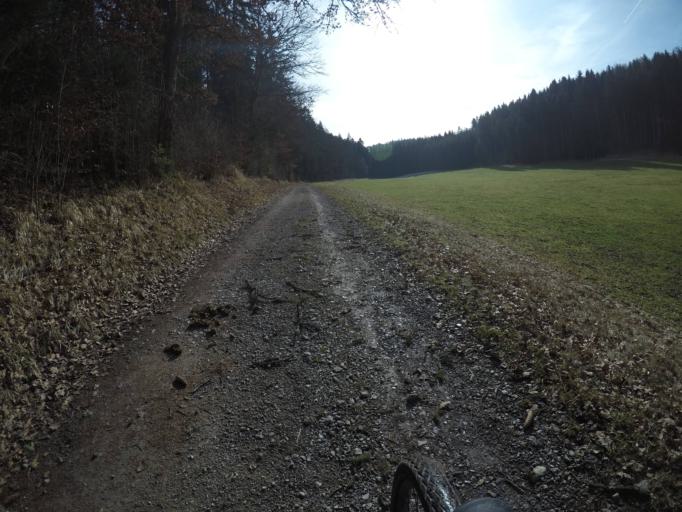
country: DE
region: Baden-Wuerttemberg
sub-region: Regierungsbezirk Stuttgart
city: Oberjettingen
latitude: 48.5998
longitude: 8.7896
